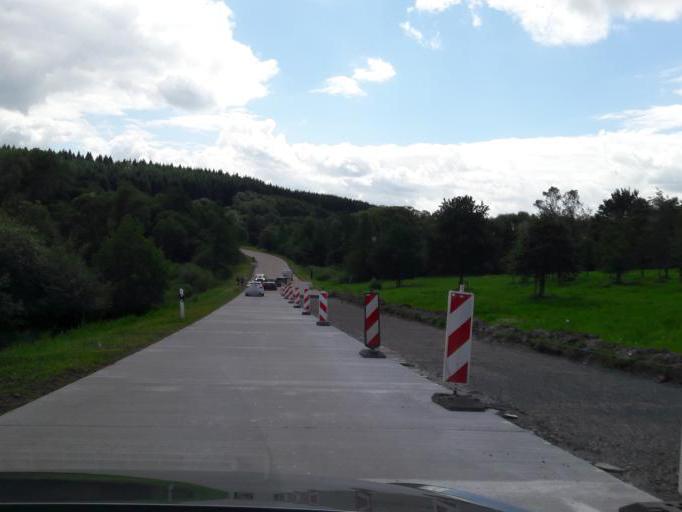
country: DE
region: Rheinland-Pfalz
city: Reichenbach
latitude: 49.6472
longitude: 7.3012
